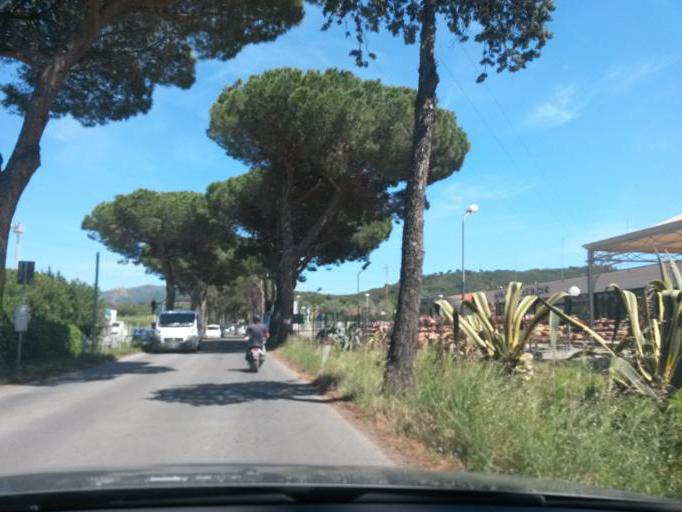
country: IT
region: Tuscany
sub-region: Provincia di Livorno
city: Portoferraio
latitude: 42.7996
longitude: 10.3178
